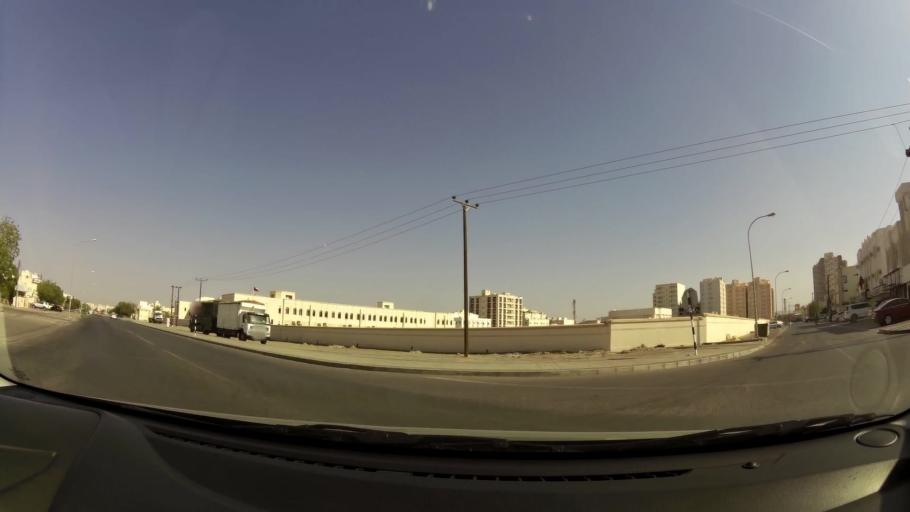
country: OM
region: Muhafazat Masqat
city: As Sib al Jadidah
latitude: 23.6288
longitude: 58.1981
